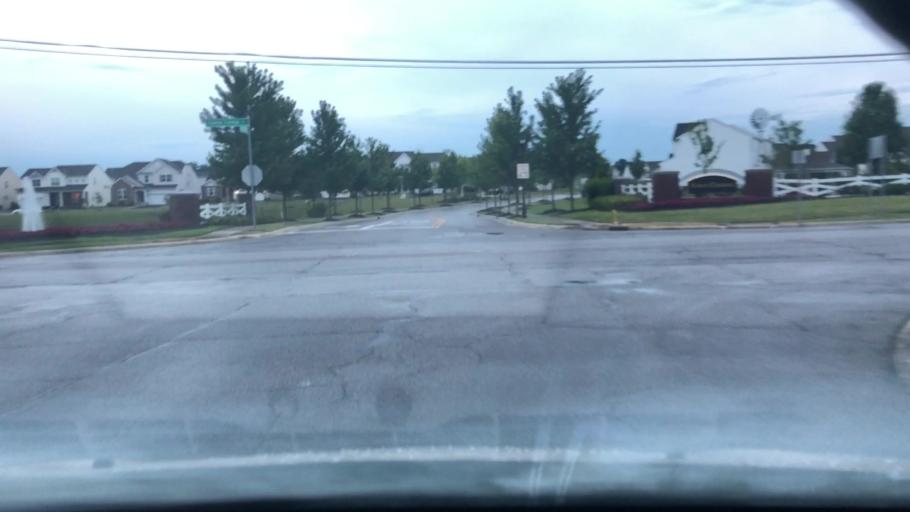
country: US
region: Ohio
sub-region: Franklin County
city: New Albany
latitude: 40.1004
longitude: -82.8544
